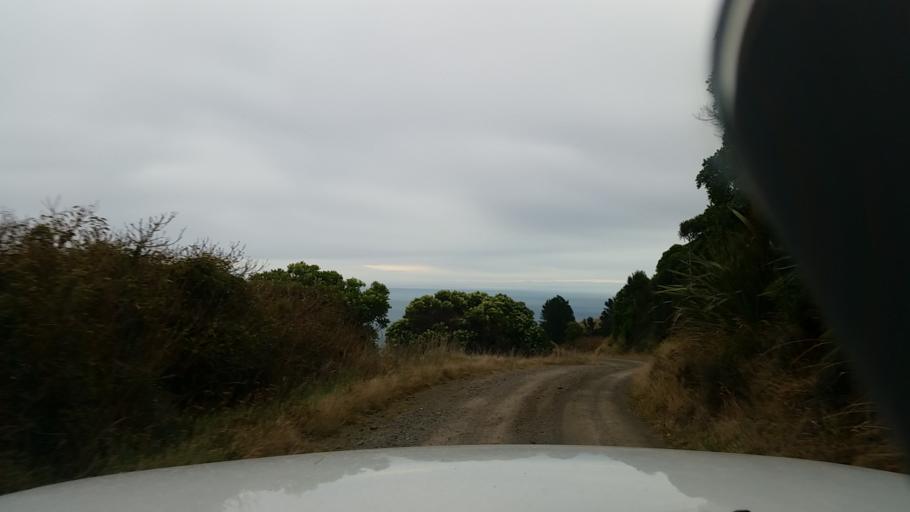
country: NZ
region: Canterbury
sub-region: Christchurch City
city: Christchurch
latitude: -43.8172
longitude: 172.7796
